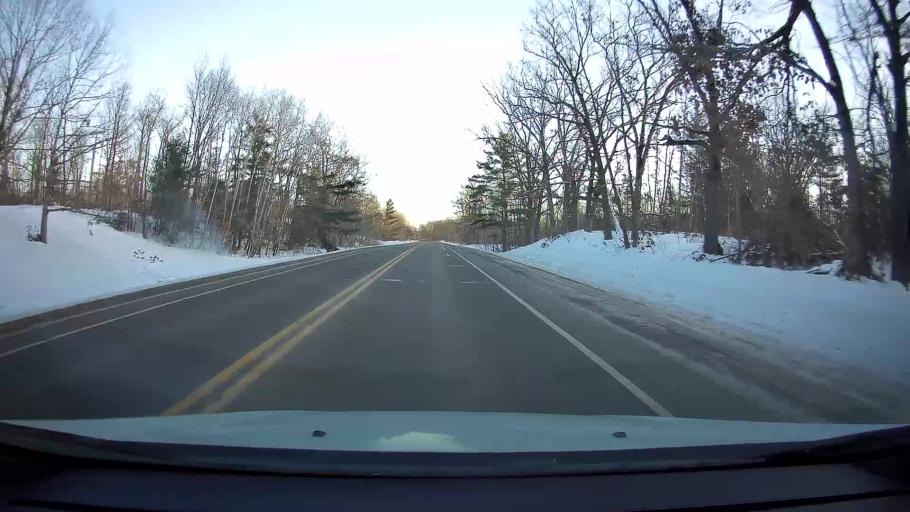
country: US
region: Wisconsin
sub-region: Barron County
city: Turtle Lake
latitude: 45.4112
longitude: -92.1358
